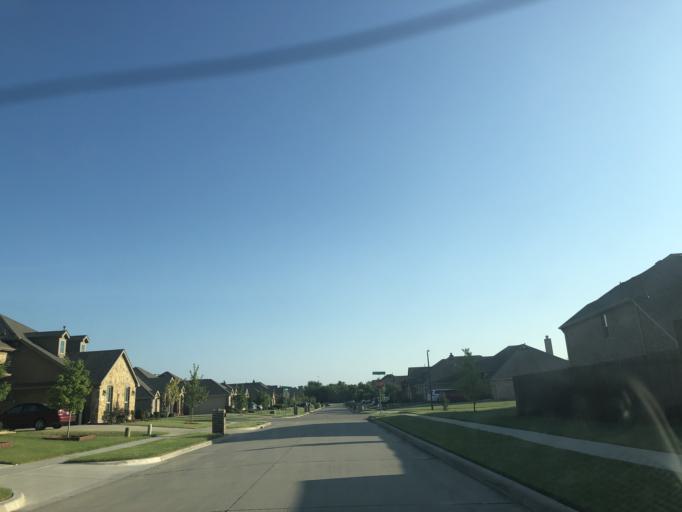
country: US
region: Texas
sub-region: Dallas County
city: Sunnyvale
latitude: 32.8429
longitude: -96.5599
